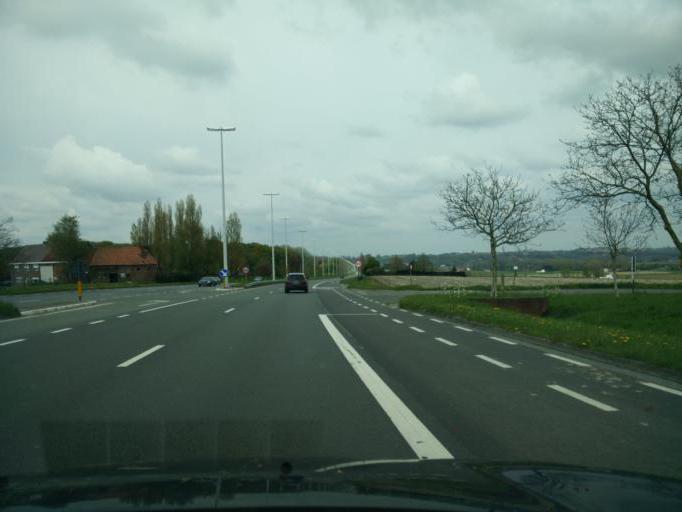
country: BE
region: Flanders
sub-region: Provincie Oost-Vlaanderen
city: Oudenaarde
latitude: 50.8004
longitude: 3.5925
